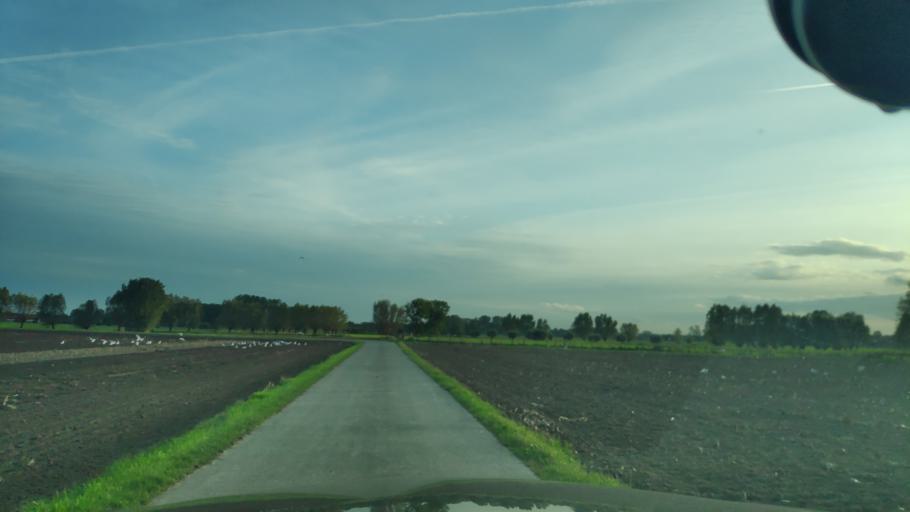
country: BE
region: Flanders
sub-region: Provincie Oost-Vlaanderen
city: Aalter
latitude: 51.1118
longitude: 3.4905
